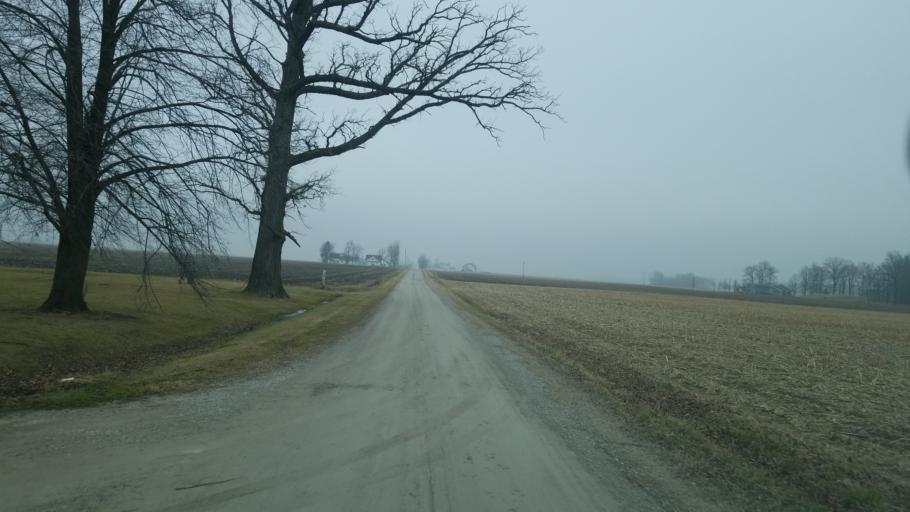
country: US
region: Indiana
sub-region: Adams County
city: Berne
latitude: 40.6959
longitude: -85.0135
